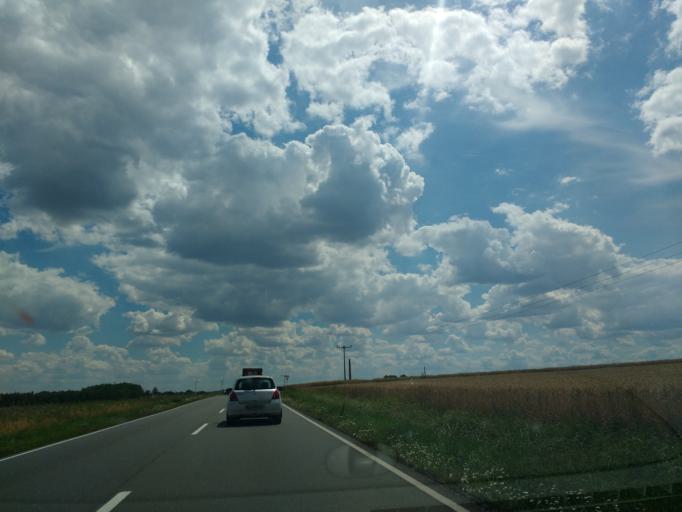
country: DE
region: Saxony-Anhalt
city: Kretzschau
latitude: 51.0623
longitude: 12.0646
